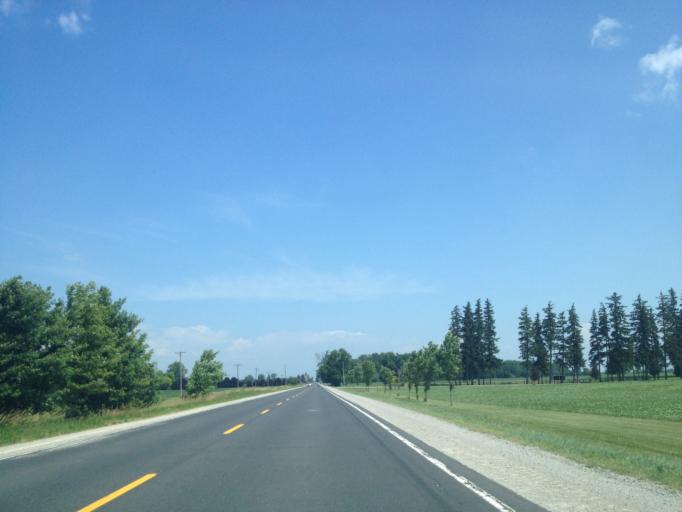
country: CA
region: Ontario
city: Stratford
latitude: 43.3319
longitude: -81.2052
